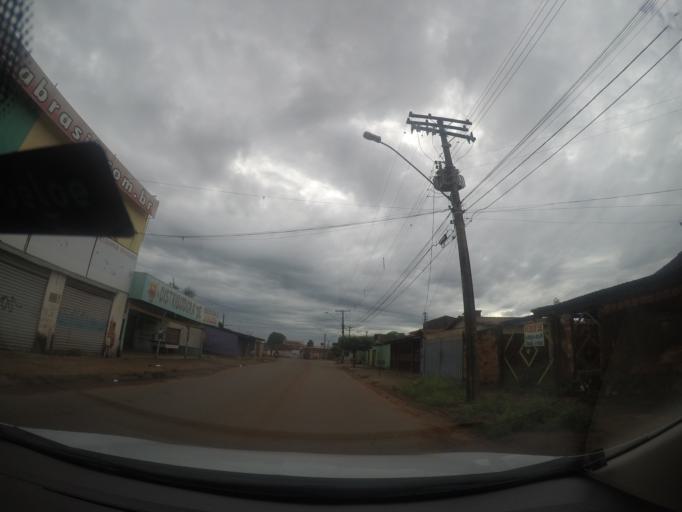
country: BR
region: Goias
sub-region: Goiania
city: Goiania
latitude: -16.6417
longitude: -49.3316
